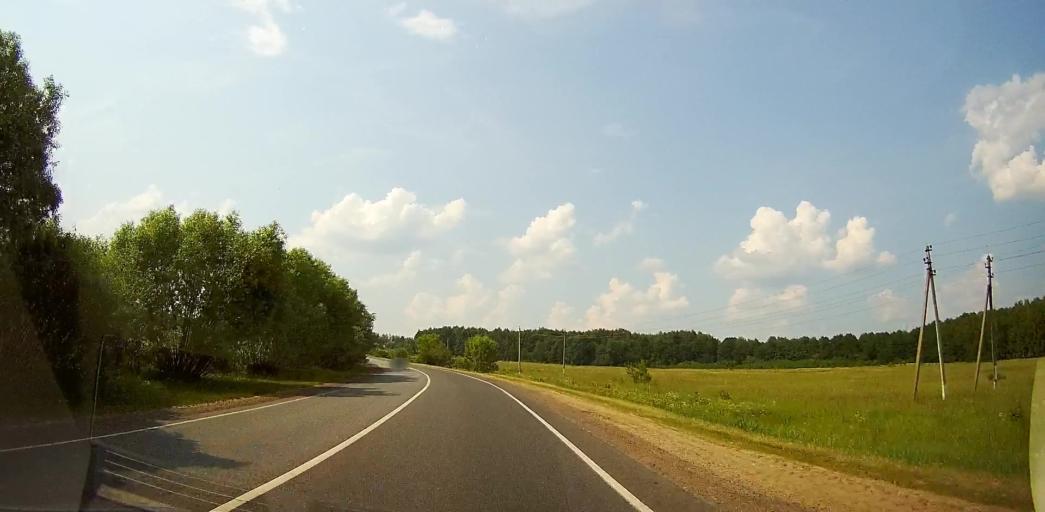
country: RU
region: Moskovskaya
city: Stupino
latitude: 54.9490
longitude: 38.1329
